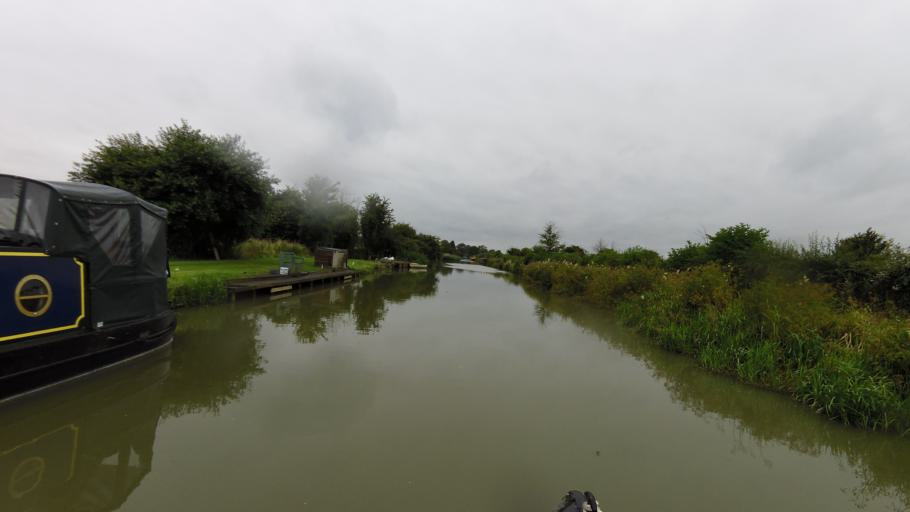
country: GB
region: England
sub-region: Wiltshire
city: Holt
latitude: 51.3433
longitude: -2.1928
